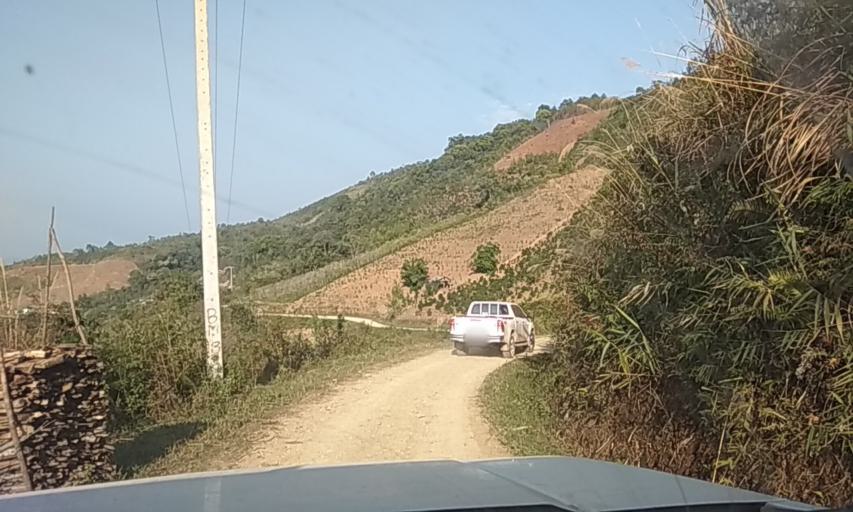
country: LA
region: Phongsali
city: Phongsali
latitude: 21.6706
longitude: 102.1840
